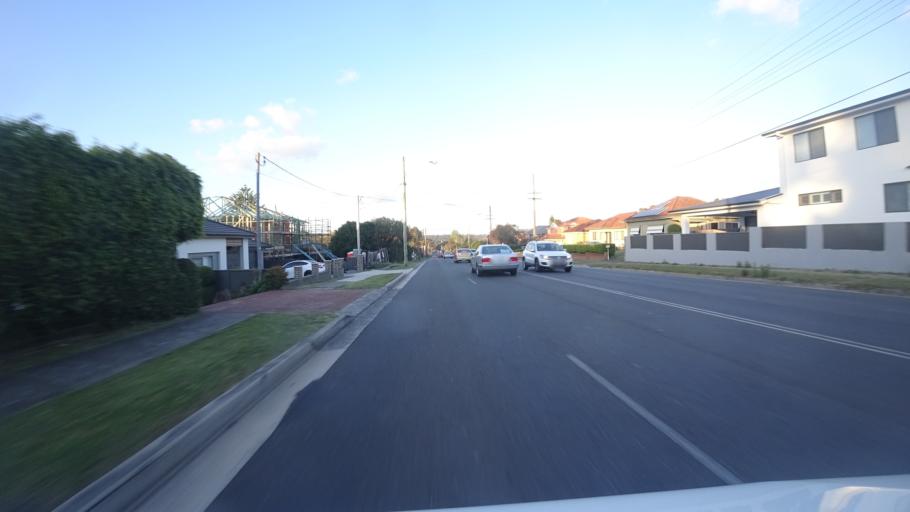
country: AU
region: New South Wales
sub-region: Ryde
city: North Ryde
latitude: -33.7958
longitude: 151.1253
